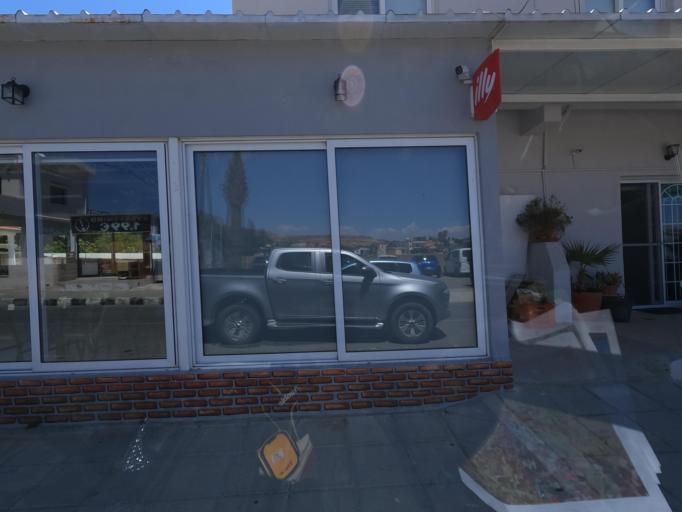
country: CY
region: Larnaka
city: Pyla
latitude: 35.0103
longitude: 33.6914
